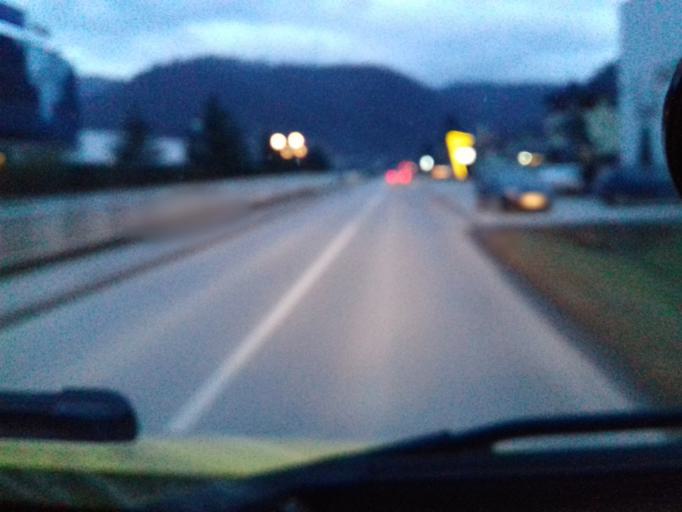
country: BA
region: Federation of Bosnia and Herzegovina
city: Dobrinje
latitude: 44.0516
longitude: 18.1085
